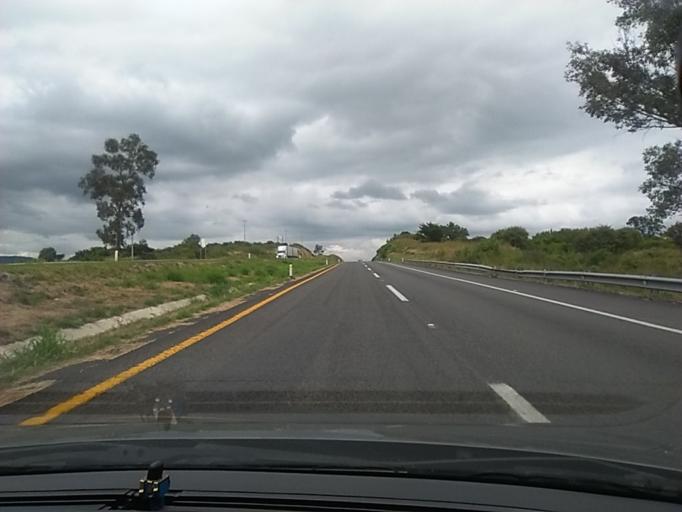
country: MX
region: Jalisco
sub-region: Zapotlanejo
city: La Mezquitera
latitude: 20.5566
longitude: -103.0647
